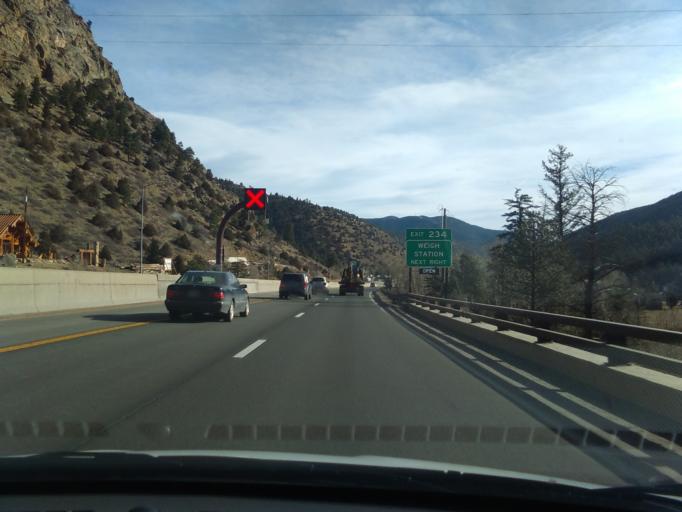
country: US
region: Colorado
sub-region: Clear Creek County
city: Georgetown
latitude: 39.7663
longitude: -105.6250
